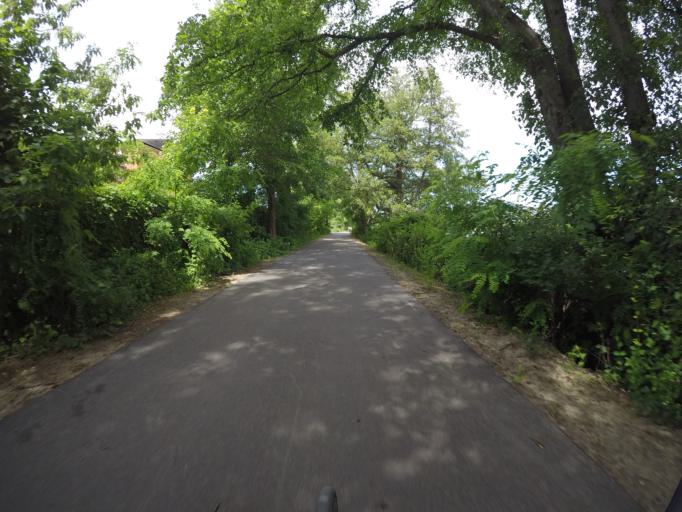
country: DE
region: Berlin
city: Kopenick Bezirk
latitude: 52.4508
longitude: 13.5669
